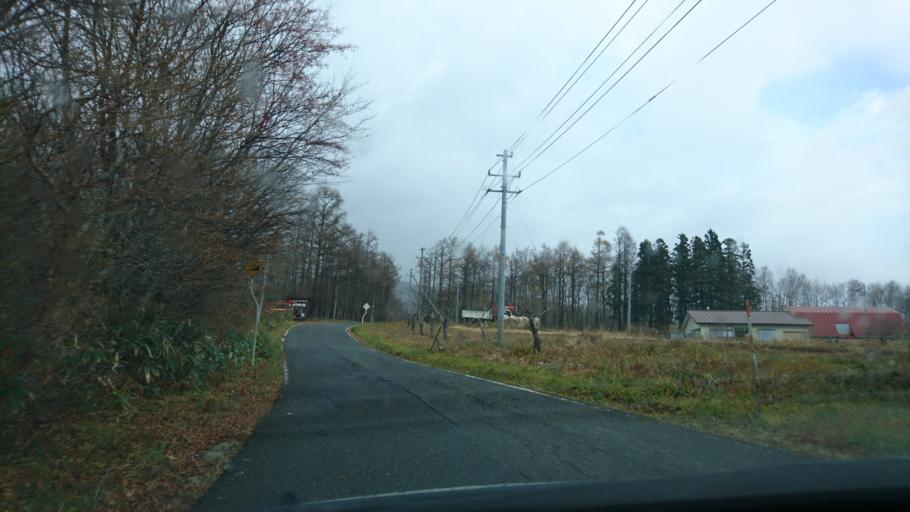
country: JP
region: Iwate
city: Ichinoseki
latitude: 38.9294
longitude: 140.8386
